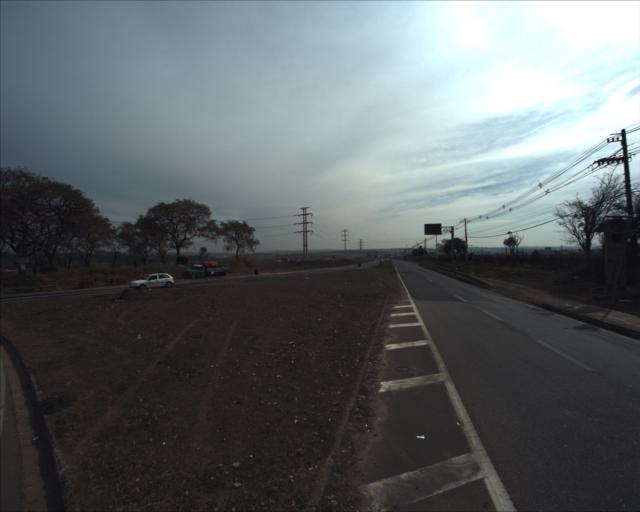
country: BR
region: Sao Paulo
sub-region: Sorocaba
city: Sorocaba
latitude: -23.4499
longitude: -47.5135
